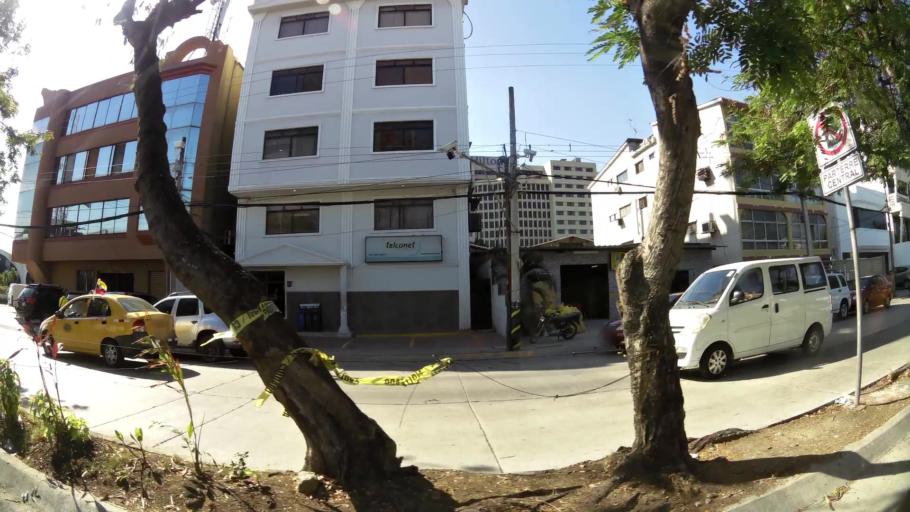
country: EC
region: Guayas
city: Eloy Alfaro
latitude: -2.1582
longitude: -79.8995
